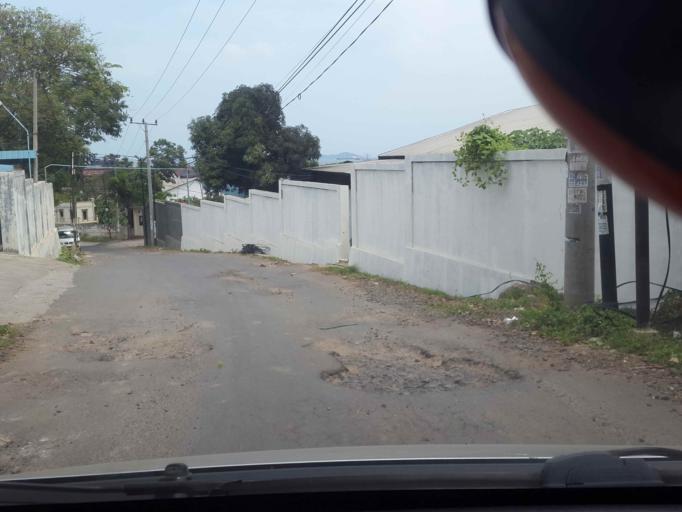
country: ID
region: Lampung
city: Panjang
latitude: -5.4402
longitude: 105.2998
